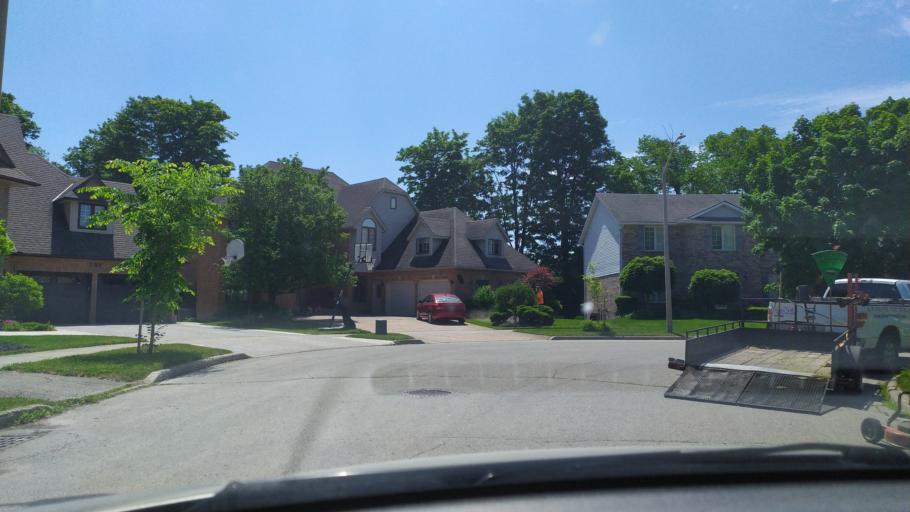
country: CA
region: Ontario
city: Waterloo
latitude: 43.4533
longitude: -80.5669
